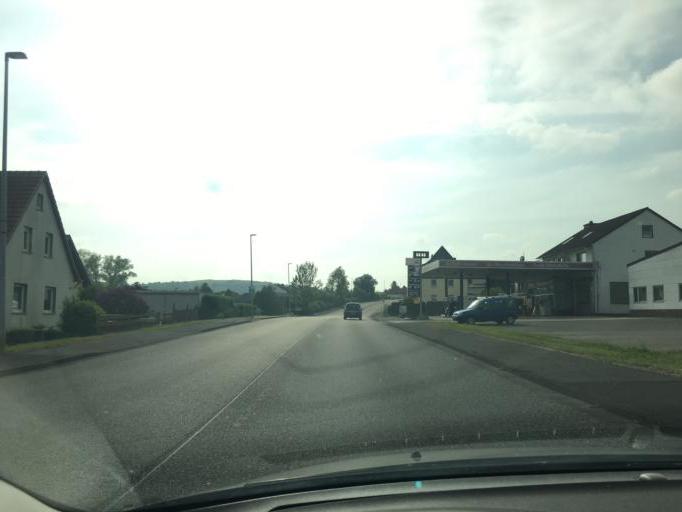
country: DE
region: Hesse
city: Hessisch Lichtenau
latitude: 51.1981
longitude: 9.7767
